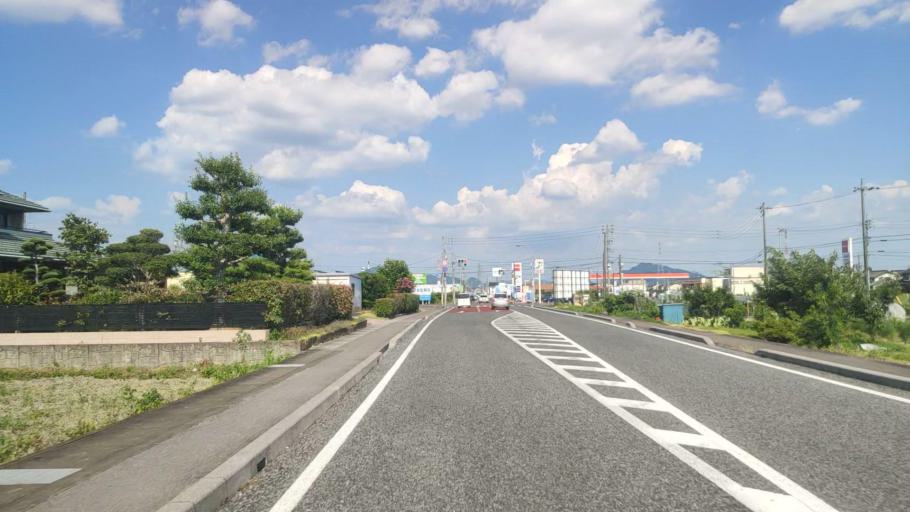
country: JP
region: Gifu
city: Gifu-shi
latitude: 35.4501
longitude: 136.6927
